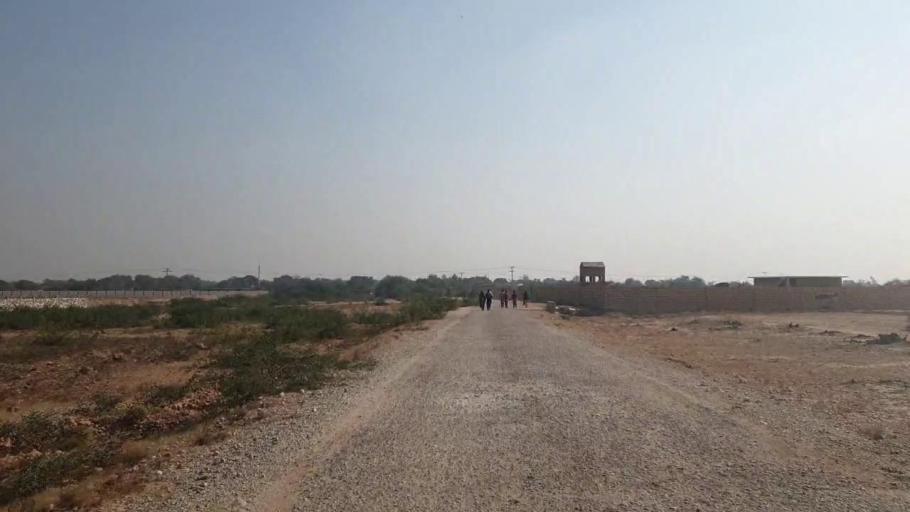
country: PK
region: Sindh
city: Kotri
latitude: 25.3235
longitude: 68.2354
